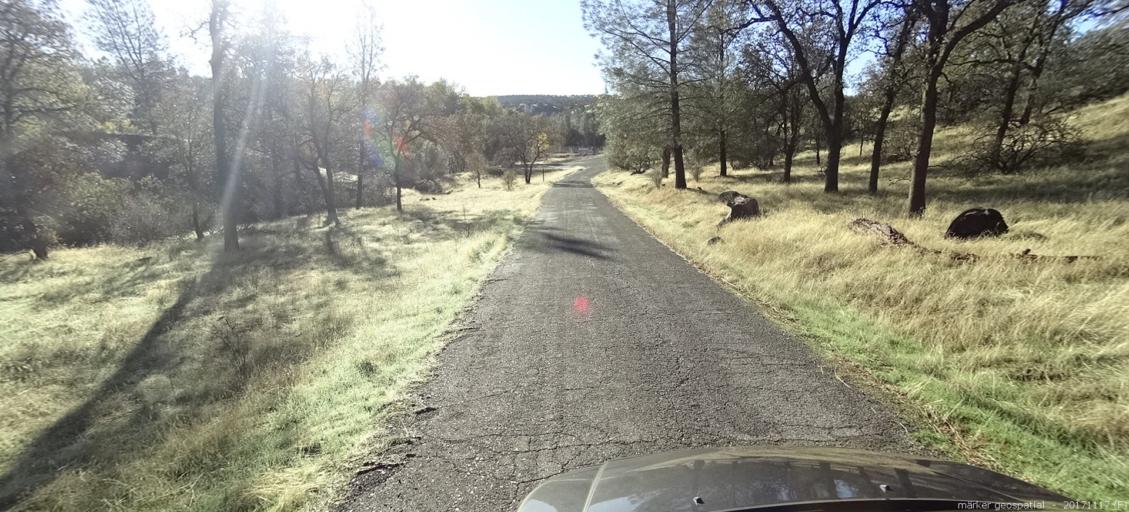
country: US
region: California
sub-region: Shasta County
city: Cottonwood
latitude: 40.4027
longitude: -122.1306
